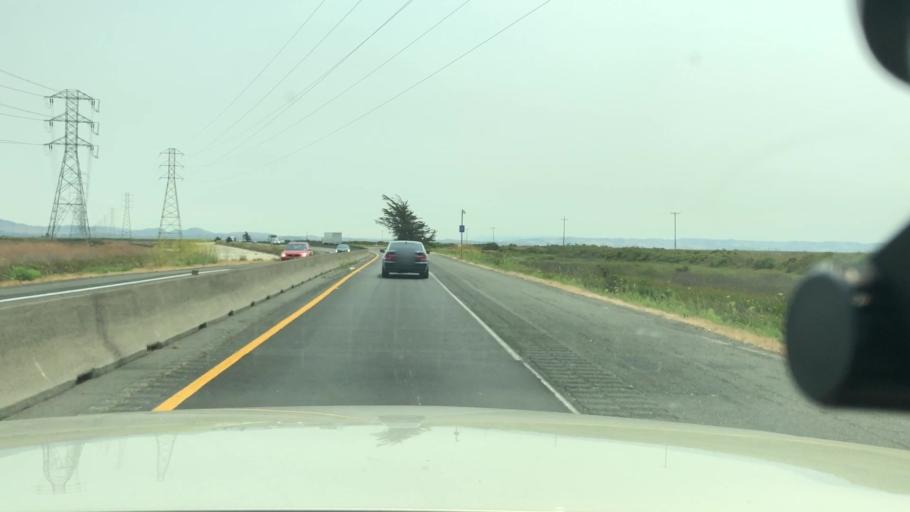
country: US
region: California
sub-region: Marin County
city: Black Point-Green Point
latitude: 38.1546
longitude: -122.4005
